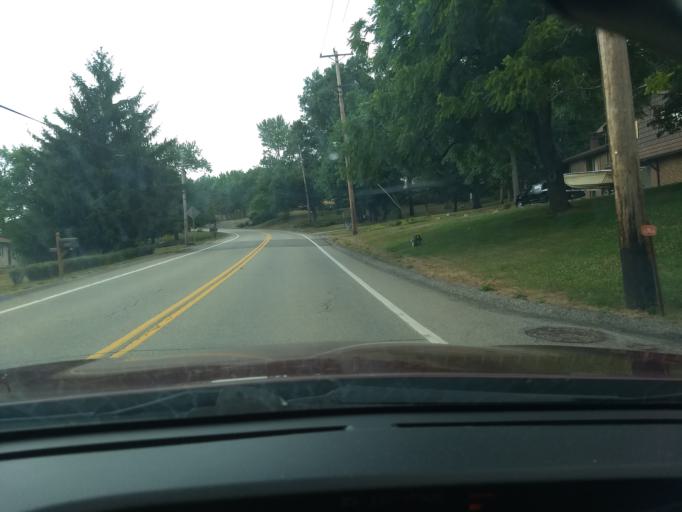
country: US
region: Pennsylvania
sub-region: Allegheny County
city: Curtisville
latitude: 40.6317
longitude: -79.8667
